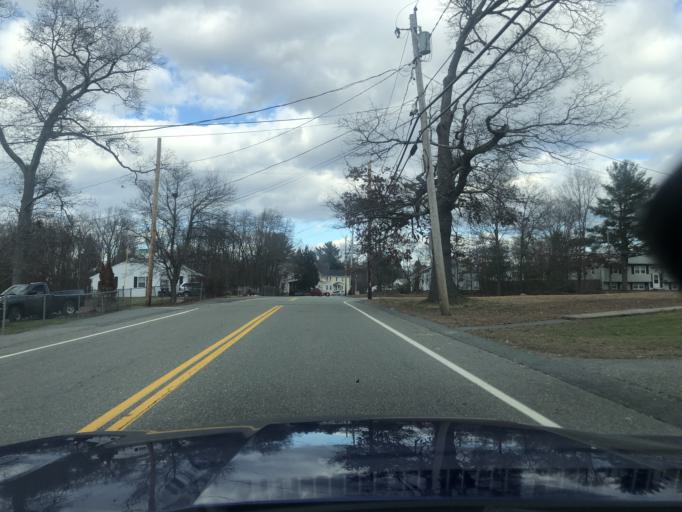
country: US
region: Massachusetts
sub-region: Plymouth County
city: Brockton
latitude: 42.1026
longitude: -71.0069
